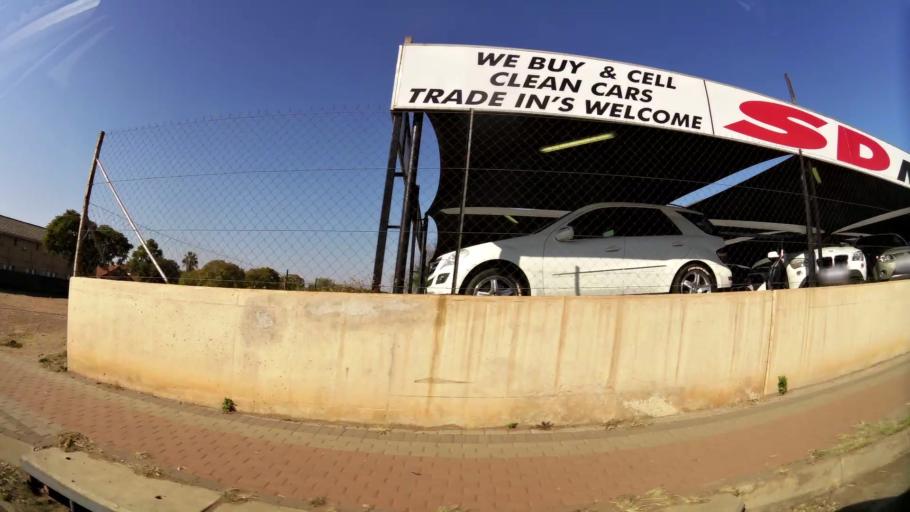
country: ZA
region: Gauteng
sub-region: City of Tshwane Metropolitan Municipality
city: Pretoria
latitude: -25.7132
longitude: 28.1862
